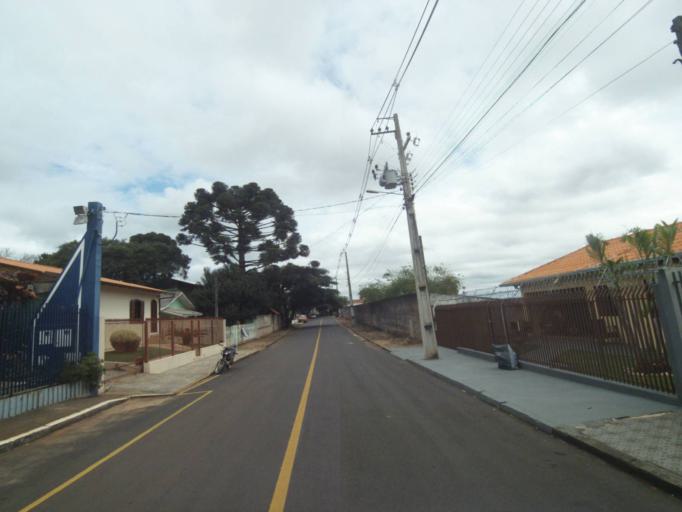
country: BR
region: Parana
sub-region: Telemaco Borba
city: Telemaco Borba
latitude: -24.3358
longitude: -50.6252
